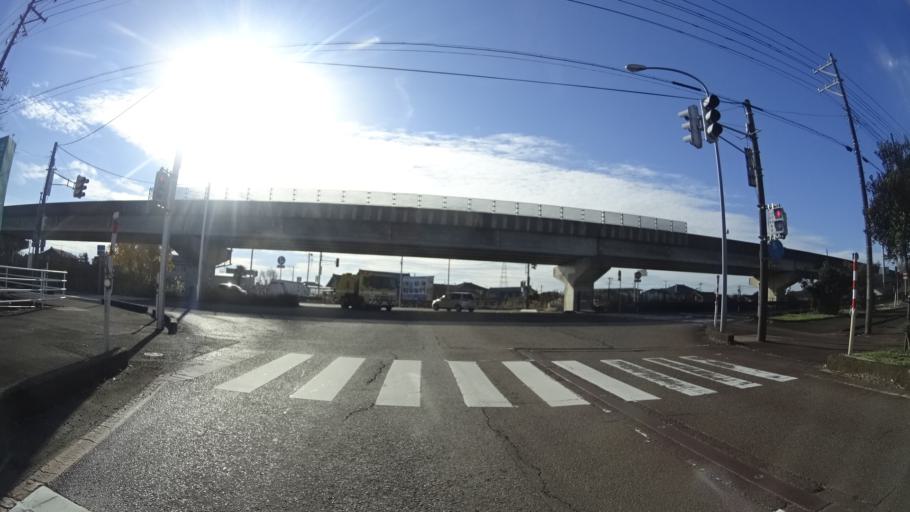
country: JP
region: Niigata
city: Yoshida-kasugacho
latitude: 37.6207
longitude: 138.8415
